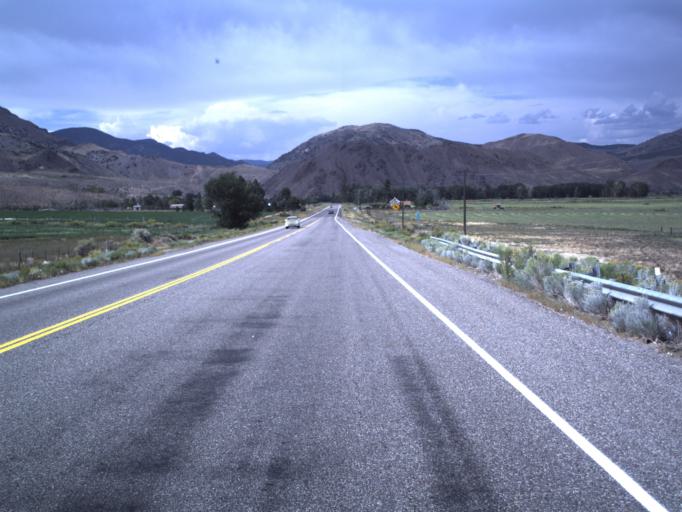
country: US
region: Utah
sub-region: Sevier County
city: Monroe
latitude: 38.4624
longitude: -112.2329
